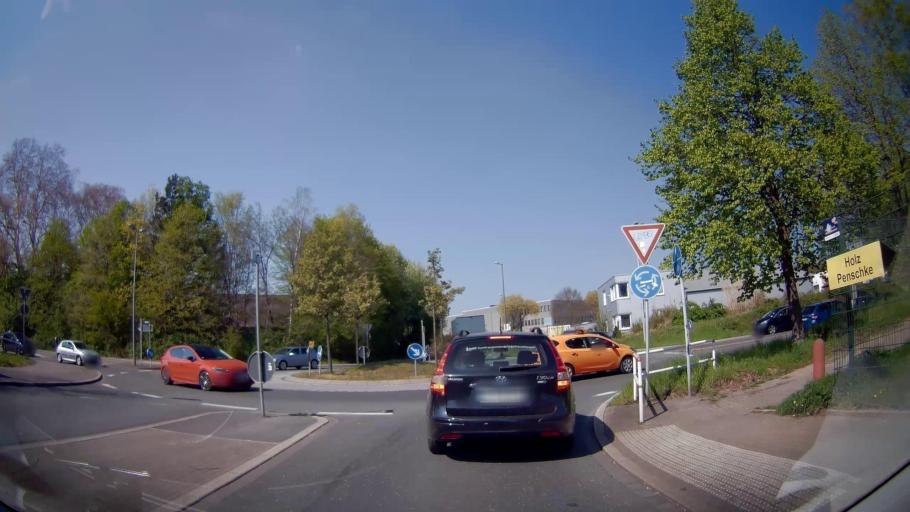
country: DE
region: North Rhine-Westphalia
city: Bochum-Hordel
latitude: 51.4861
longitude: 7.1658
